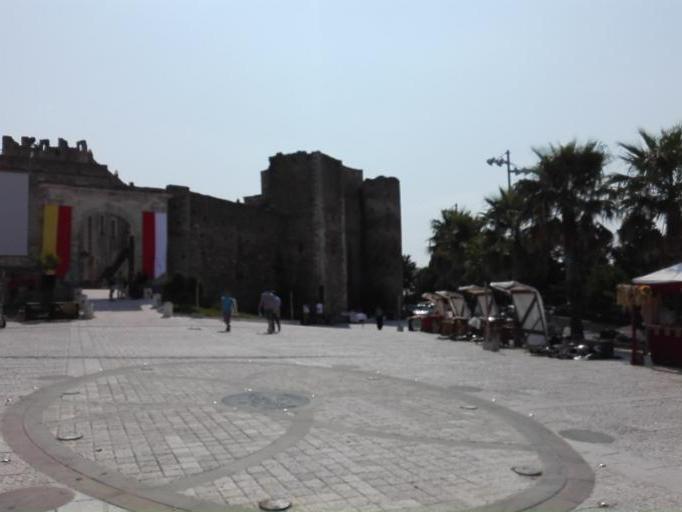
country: IT
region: Basilicate
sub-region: Provincia di Matera
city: Miglionico
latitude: 40.5682
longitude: 16.5004
